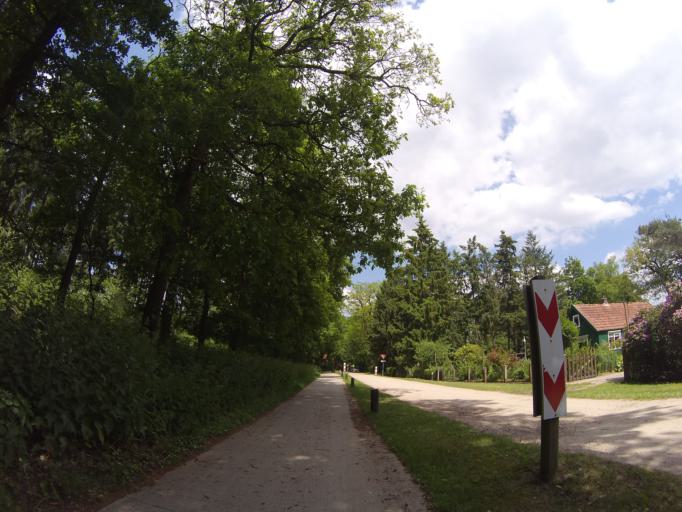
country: NL
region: Gelderland
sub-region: Gemeente Ede
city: Harskamp
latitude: 52.1794
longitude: 5.7649
